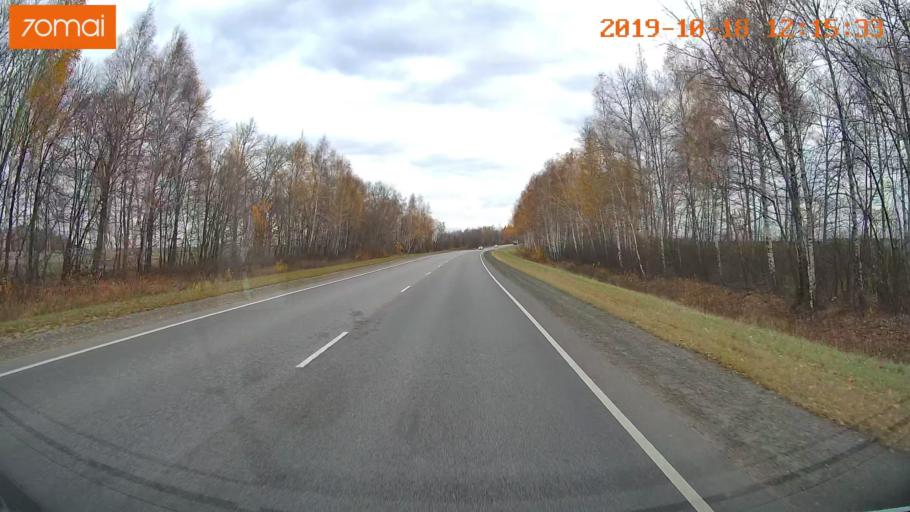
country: RU
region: Rjazan
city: Zakharovo
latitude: 54.4447
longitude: 39.4018
